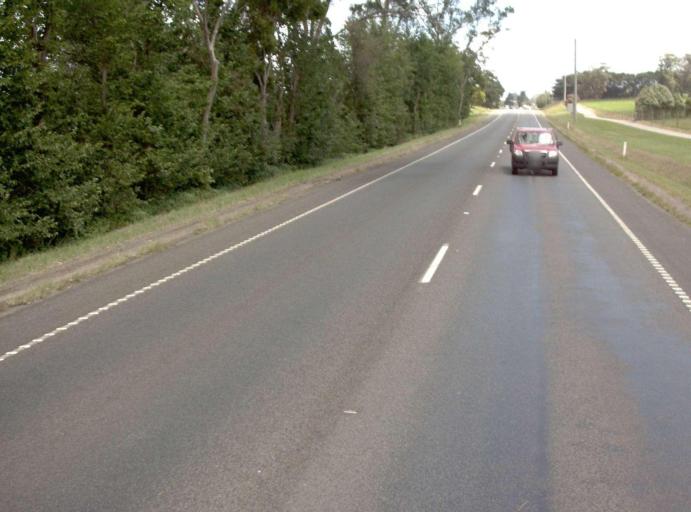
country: AU
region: Victoria
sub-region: Baw Baw
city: Warragul
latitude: -38.1476
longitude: 145.9002
